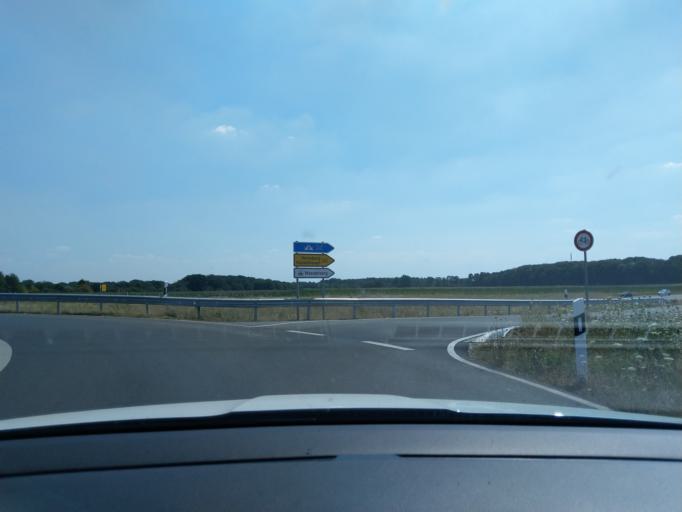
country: DE
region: North Rhine-Westphalia
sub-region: Regierungsbezirk Koln
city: Wassenberg
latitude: 51.0975
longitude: 6.2003
